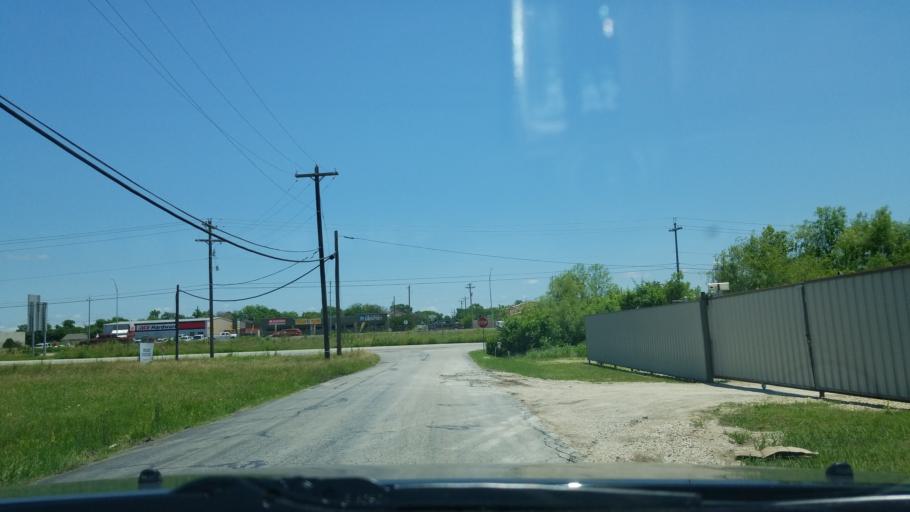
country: US
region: Texas
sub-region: Denton County
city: Sanger
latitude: 33.3566
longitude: -97.1835
